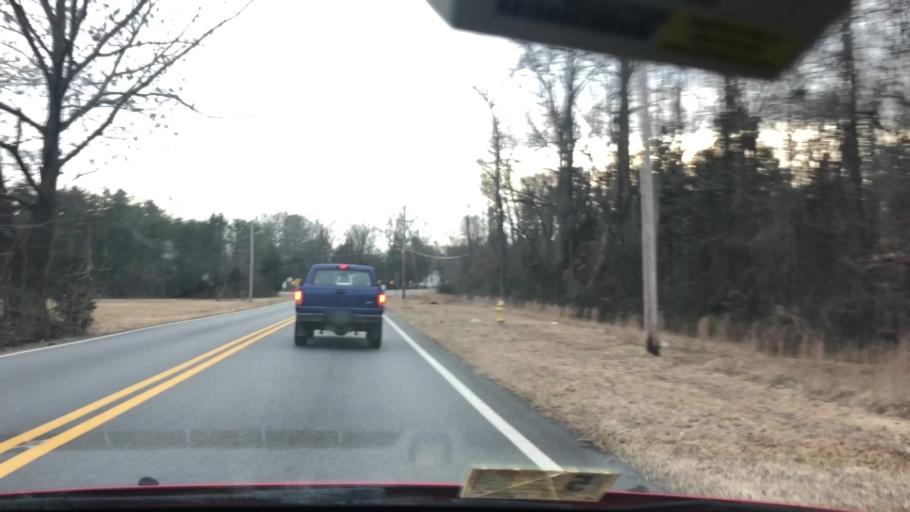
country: US
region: Maryland
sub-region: Charles County
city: Bryans Road
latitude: 38.6035
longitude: -77.0774
